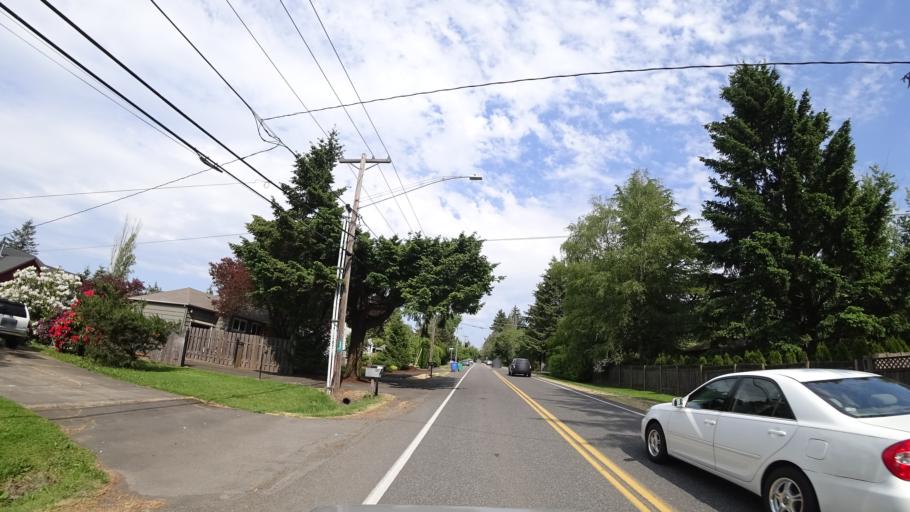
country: US
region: Oregon
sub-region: Washington County
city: Metzger
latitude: 45.4548
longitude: -122.7351
